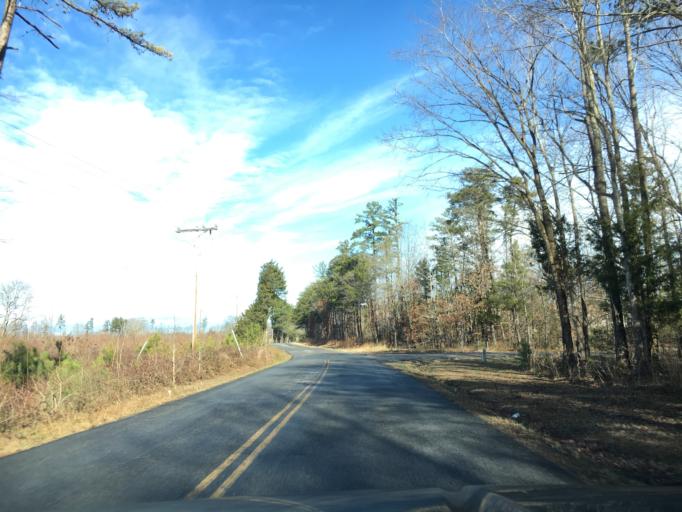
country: US
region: Virginia
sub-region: Cumberland County
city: Cumberland
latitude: 37.3565
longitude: -78.1555
